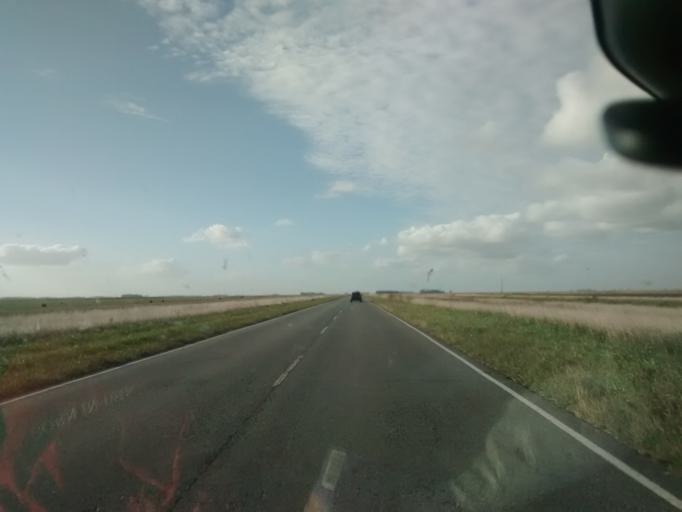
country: AR
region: Buenos Aires
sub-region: Partido de Rauch
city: Rauch
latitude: -36.5109
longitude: -58.5701
